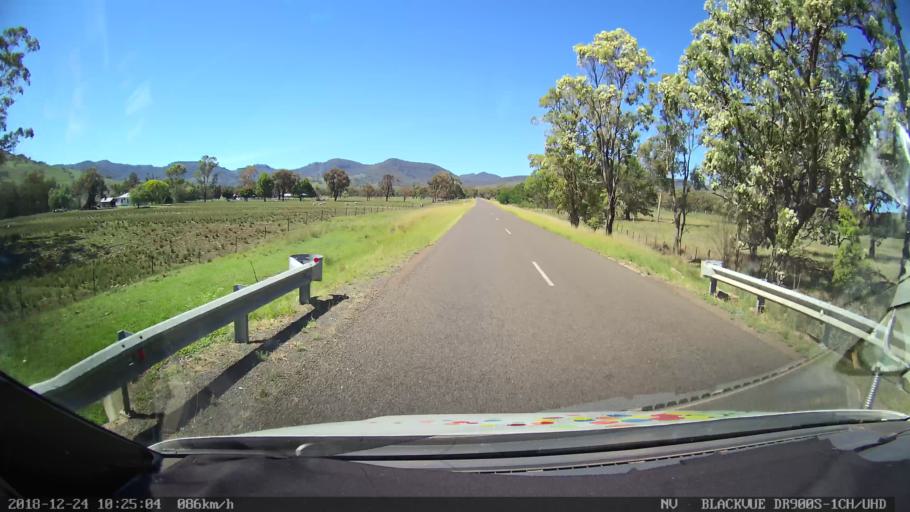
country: AU
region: New South Wales
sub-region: Liverpool Plains
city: Quirindi
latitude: -31.7944
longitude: 150.5301
